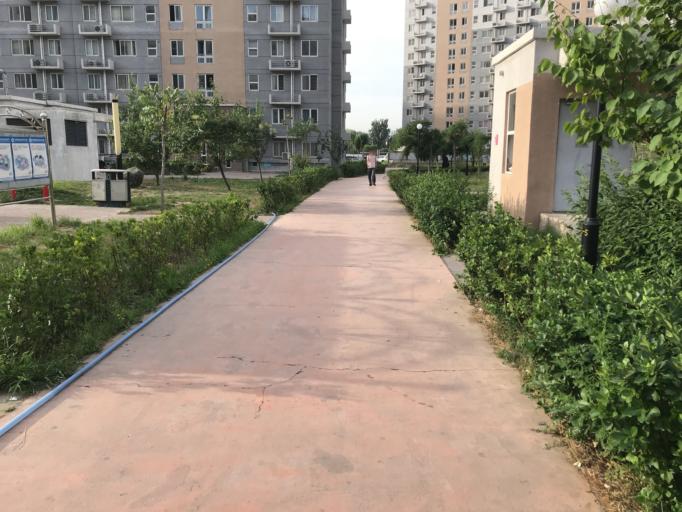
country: CN
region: Beijing
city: Shahe
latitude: 40.1230
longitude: 116.2086
